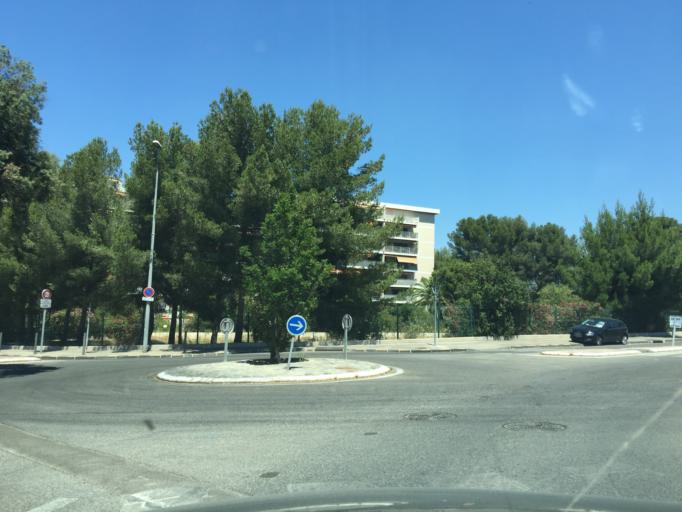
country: FR
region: Provence-Alpes-Cote d'Azur
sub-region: Departement des Bouches-du-Rhone
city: Marseille 08
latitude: 43.2385
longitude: 5.3735
